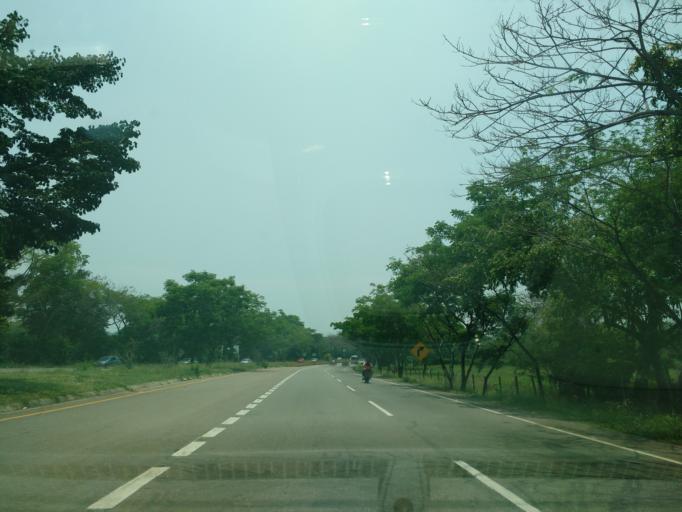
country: CO
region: Tolima
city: Melgar
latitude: 4.2131
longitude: -74.6746
